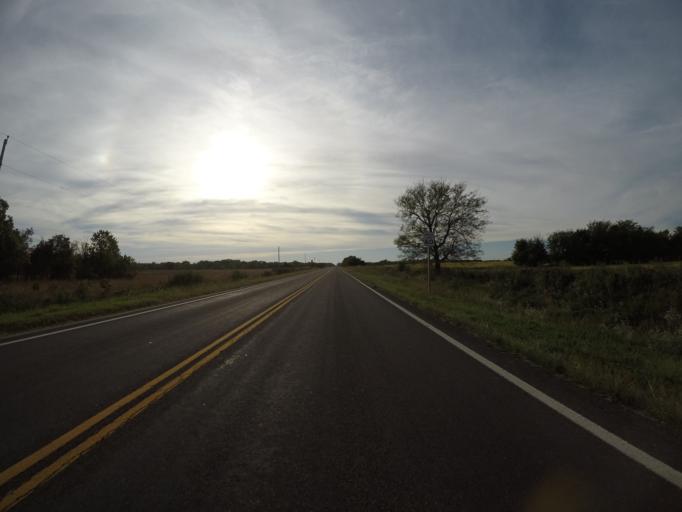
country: US
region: Kansas
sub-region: Douglas County
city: Baldwin City
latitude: 38.7824
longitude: -95.2737
